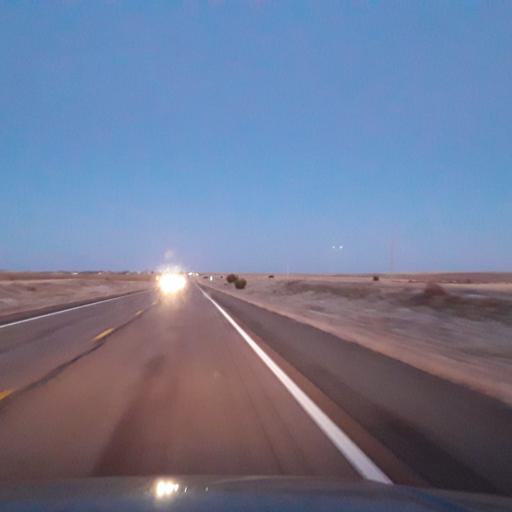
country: US
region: New Mexico
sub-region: Guadalupe County
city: Santa Rosa
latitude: 34.7711
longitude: -104.9648
